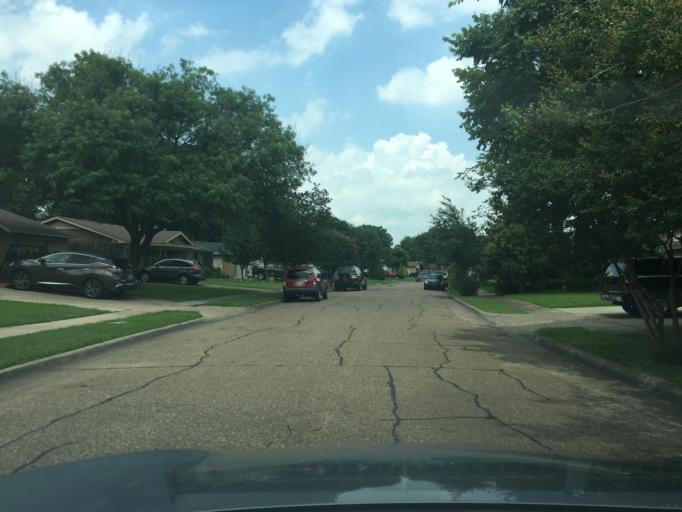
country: US
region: Texas
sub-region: Dallas County
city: Richardson
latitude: 32.9147
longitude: -96.6956
